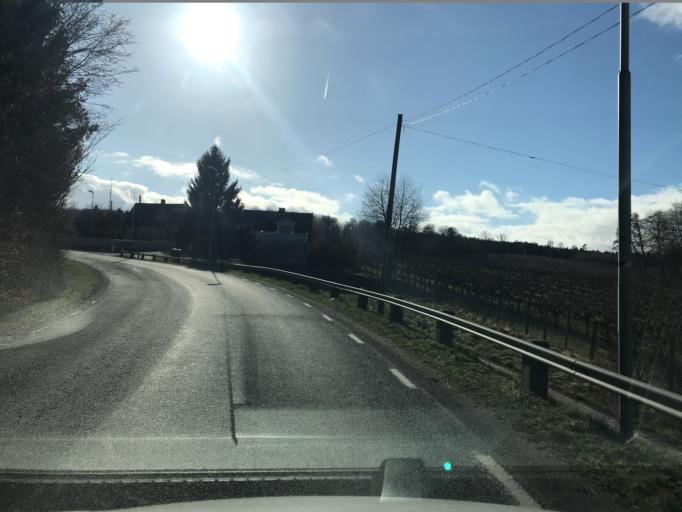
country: SE
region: Skane
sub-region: Kristianstads Kommun
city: Degeberga
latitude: 55.8844
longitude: 14.0135
